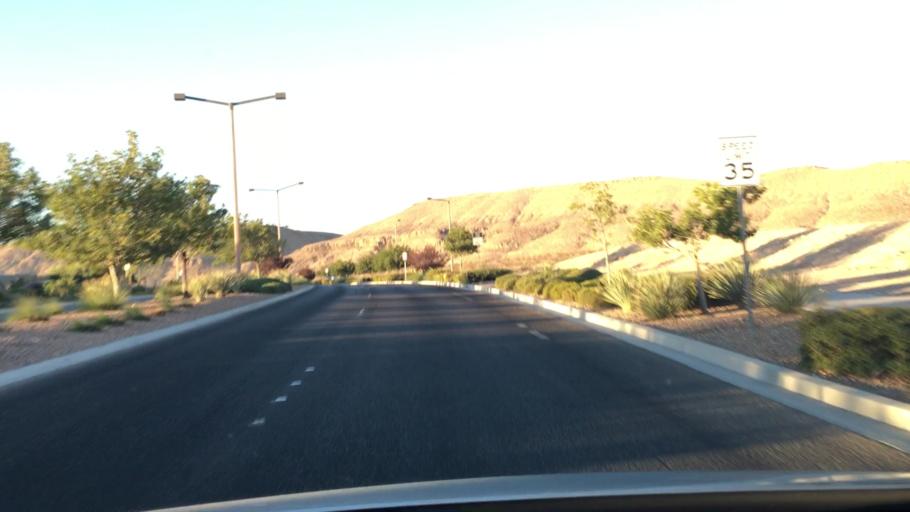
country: US
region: Nevada
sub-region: Clark County
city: Summerlin South
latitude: 36.0992
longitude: -115.3250
